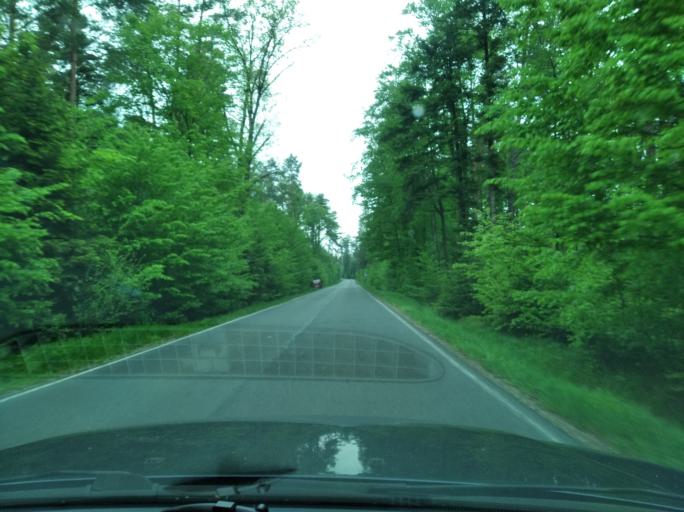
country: PL
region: Subcarpathian Voivodeship
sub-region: Powiat kolbuszowski
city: Kolbuszowa
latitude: 50.1658
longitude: 21.7596
